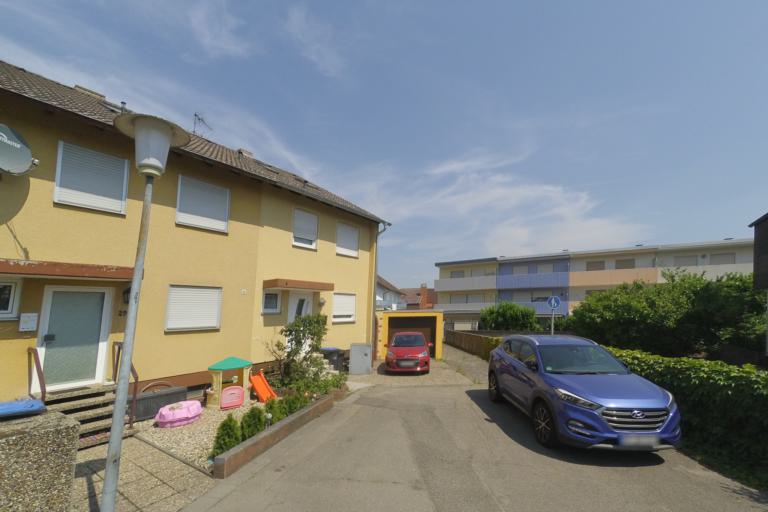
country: DE
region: Rheinland-Pfalz
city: Schifferstadt
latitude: 49.3960
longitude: 8.3696
